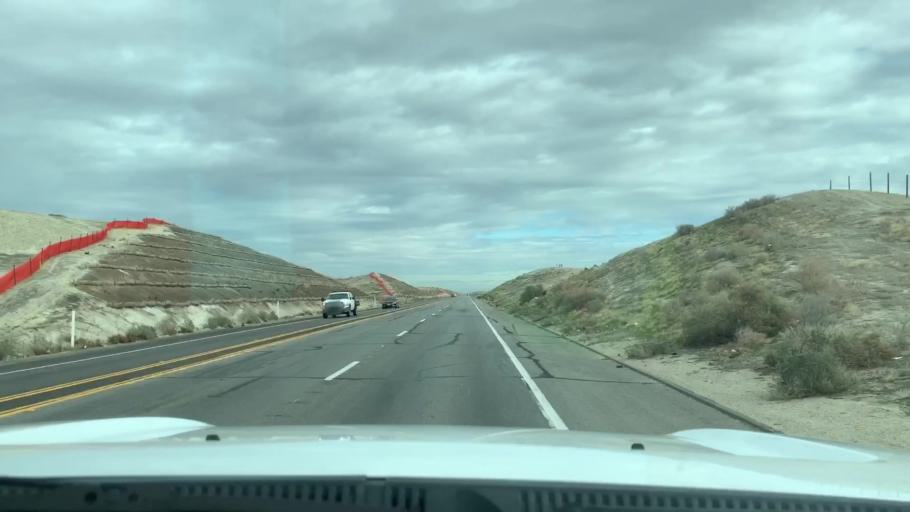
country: US
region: California
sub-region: Kern County
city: Ford City
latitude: 35.2417
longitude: -119.3546
